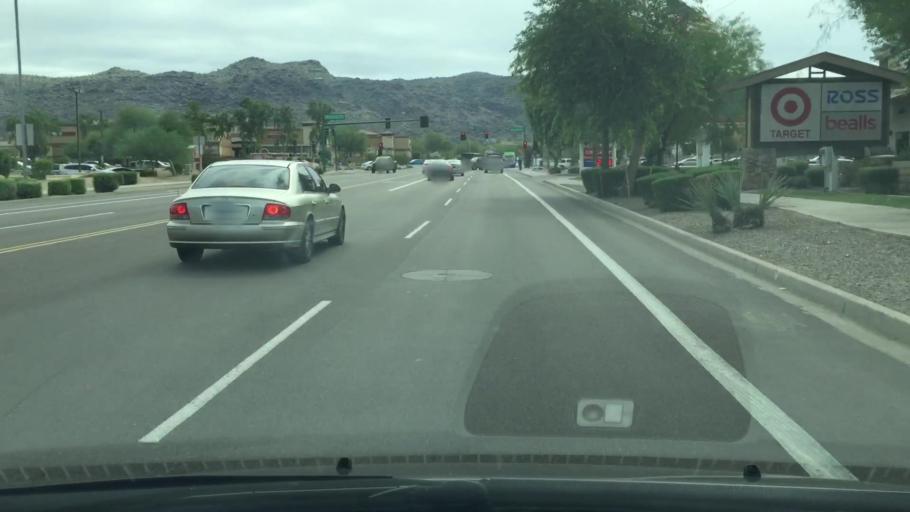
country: US
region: Arizona
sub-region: Maricopa County
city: Guadalupe
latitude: 33.3790
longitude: -112.0304
